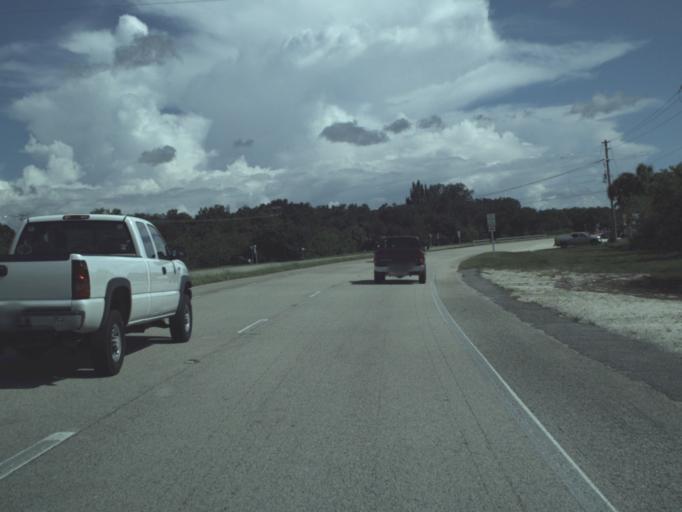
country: US
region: Florida
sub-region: Manatee County
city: Memphis
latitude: 27.5660
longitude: -82.5661
